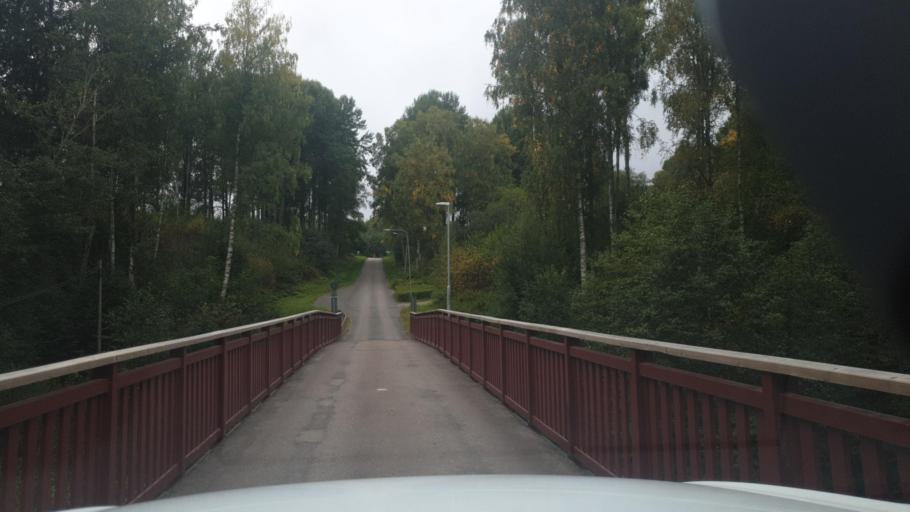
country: SE
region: Vaermland
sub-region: Sunne Kommun
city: Sunne
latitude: 59.7947
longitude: 13.1264
